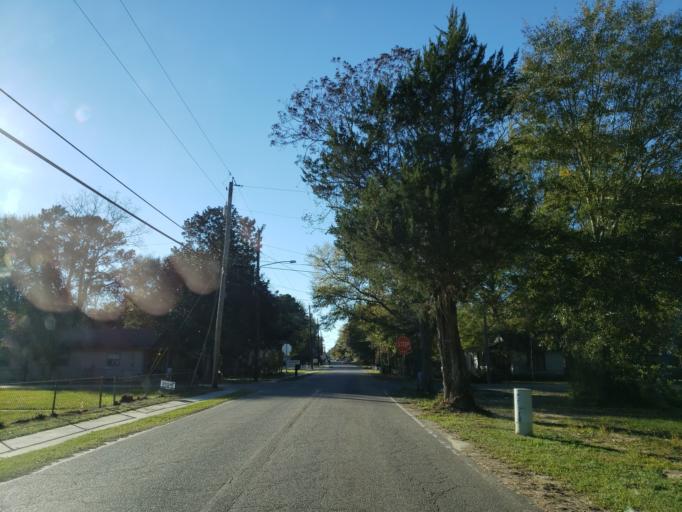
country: US
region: Mississippi
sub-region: Forrest County
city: Hattiesburg
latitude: 31.2773
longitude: -89.2731
